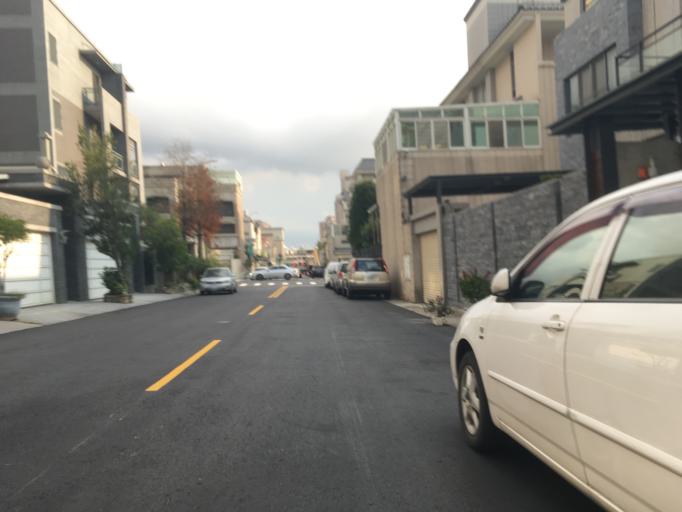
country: TW
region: Taiwan
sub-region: Taichung City
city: Taichung
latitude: 24.1807
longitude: 120.7169
